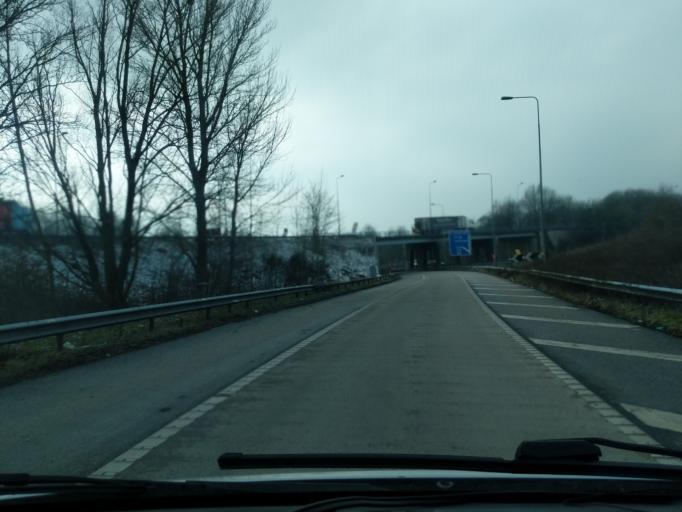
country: GB
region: England
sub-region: Manchester
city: Swinton
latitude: 53.4875
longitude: -2.3748
